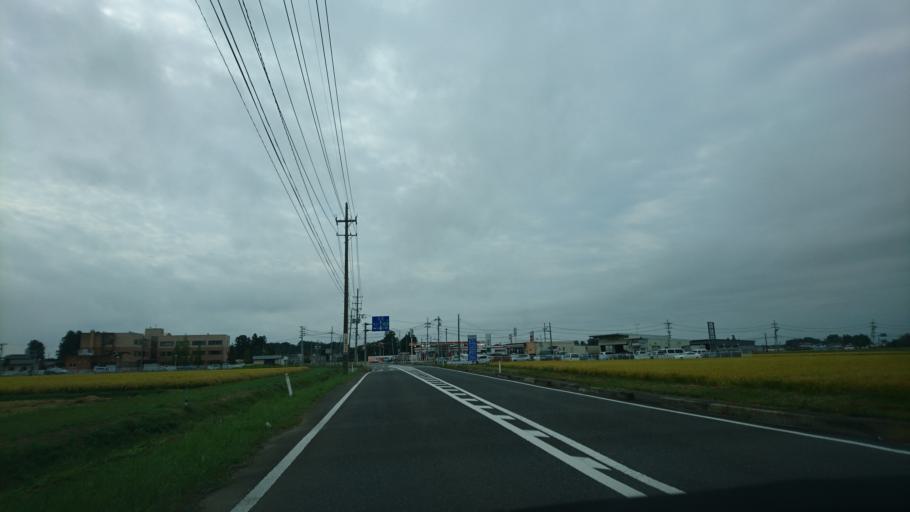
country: JP
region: Iwate
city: Ichinoseki
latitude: 38.7859
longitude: 141.1173
